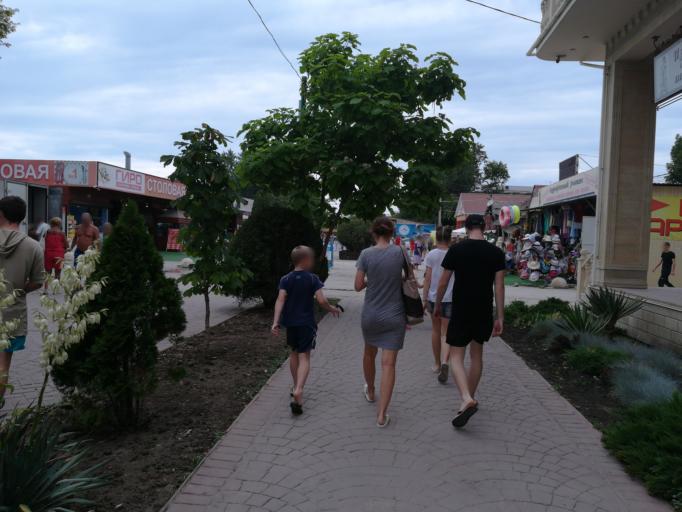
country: RU
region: Krasnodarskiy
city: Vityazevo
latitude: 44.9856
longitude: 37.2545
